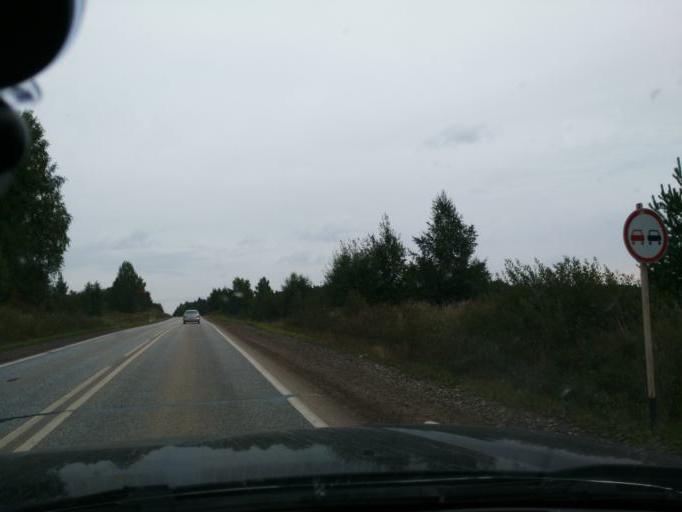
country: RU
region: Perm
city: Chernushka
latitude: 56.5765
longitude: 56.1345
